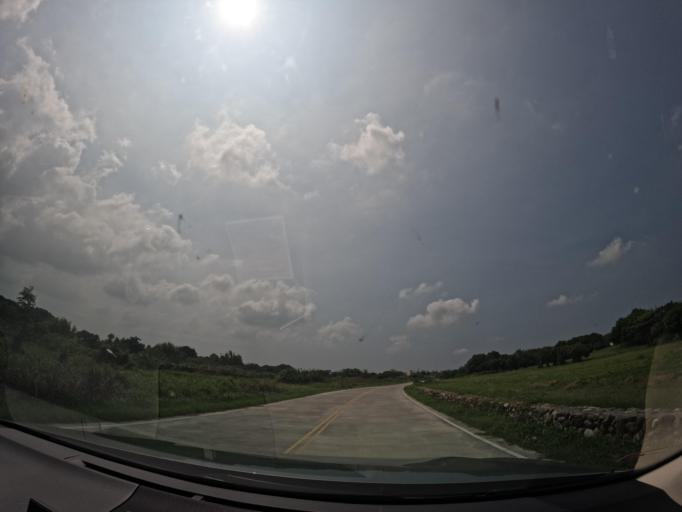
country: TW
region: Taiwan
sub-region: Chiayi
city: Taibao
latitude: 23.5642
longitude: 120.3078
